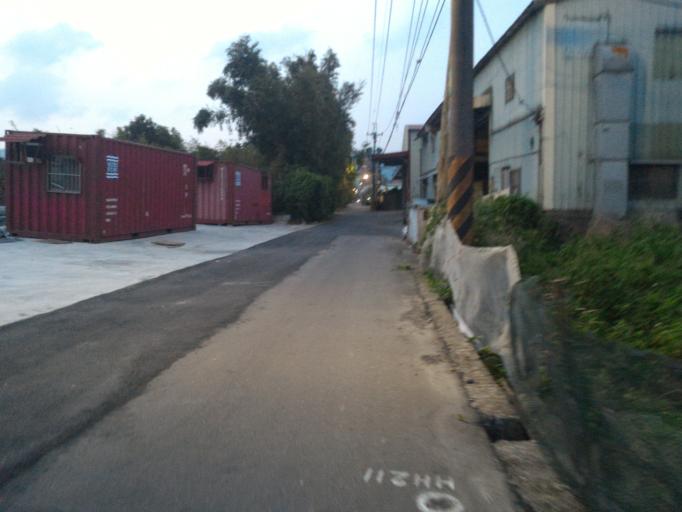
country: TW
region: Taipei
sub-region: Taipei
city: Banqiao
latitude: 24.9565
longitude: 121.4029
